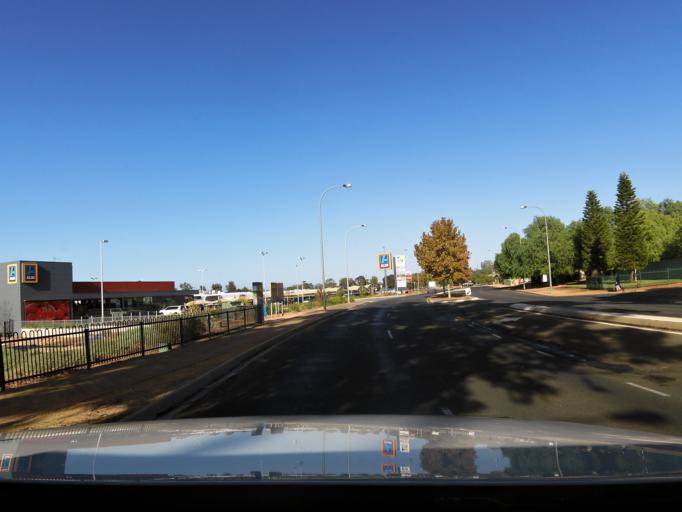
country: AU
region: South Australia
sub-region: Berri and Barmera
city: Berri
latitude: -34.2784
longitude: 140.6096
